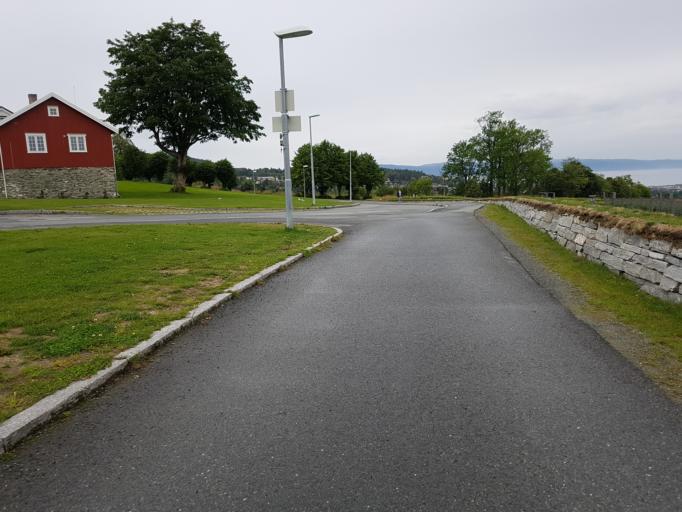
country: NO
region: Sor-Trondelag
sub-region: Trondheim
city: Trondheim
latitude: 63.4053
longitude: 10.3711
